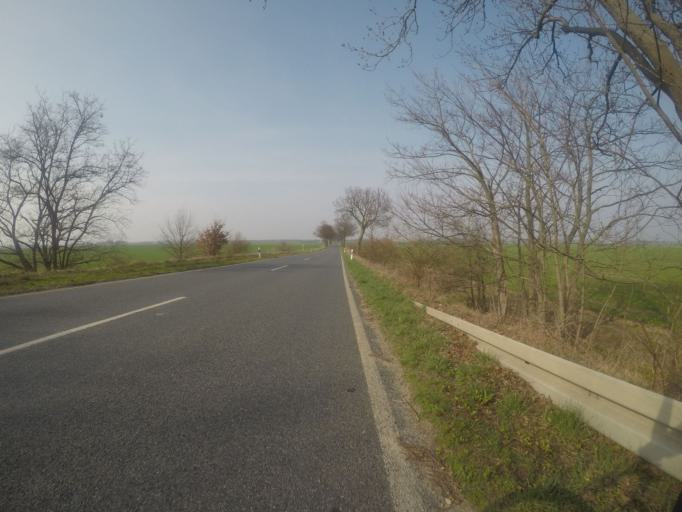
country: DE
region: Brandenburg
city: Schonefeld
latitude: 52.3208
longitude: 13.5074
